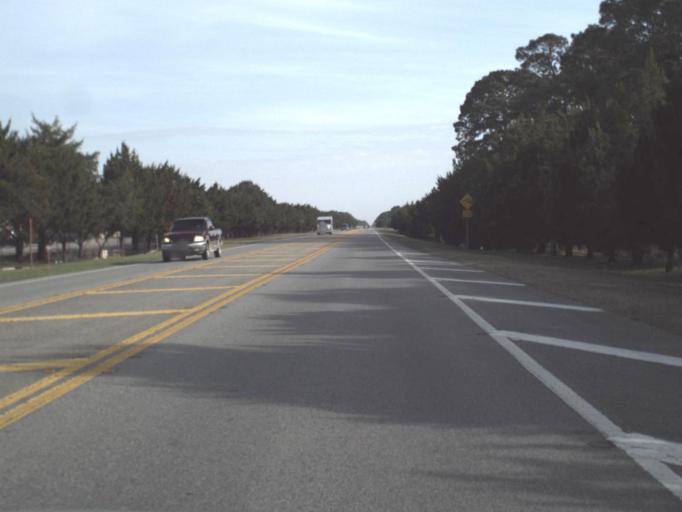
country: US
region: Florida
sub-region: Bay County
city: Tyndall Air Force Base
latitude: 30.0689
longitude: -85.5890
